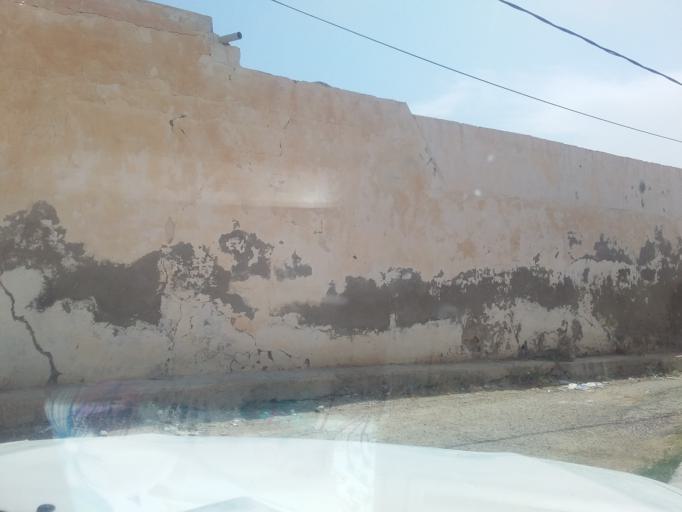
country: TN
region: Madanin
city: Medenine
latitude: 33.5852
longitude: 10.3223
